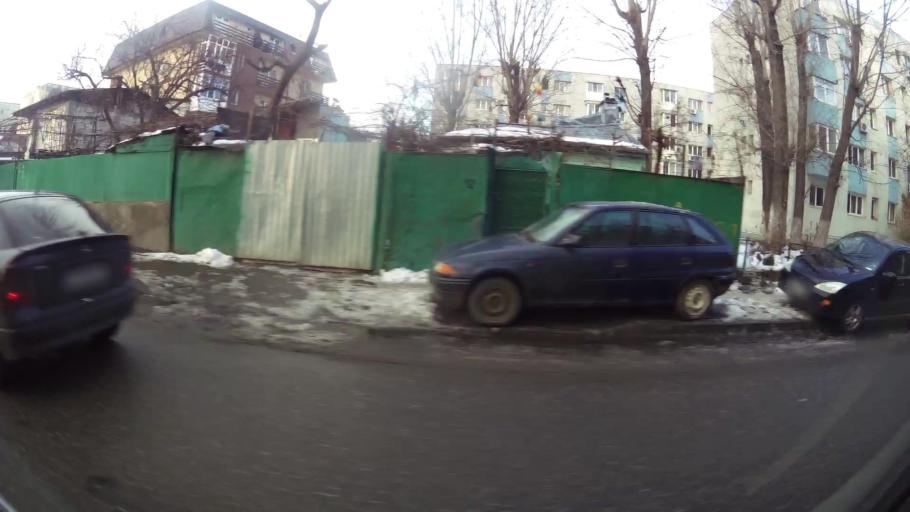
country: RO
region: Bucuresti
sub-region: Municipiul Bucuresti
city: Bucuresti
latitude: 44.3894
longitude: 26.0749
